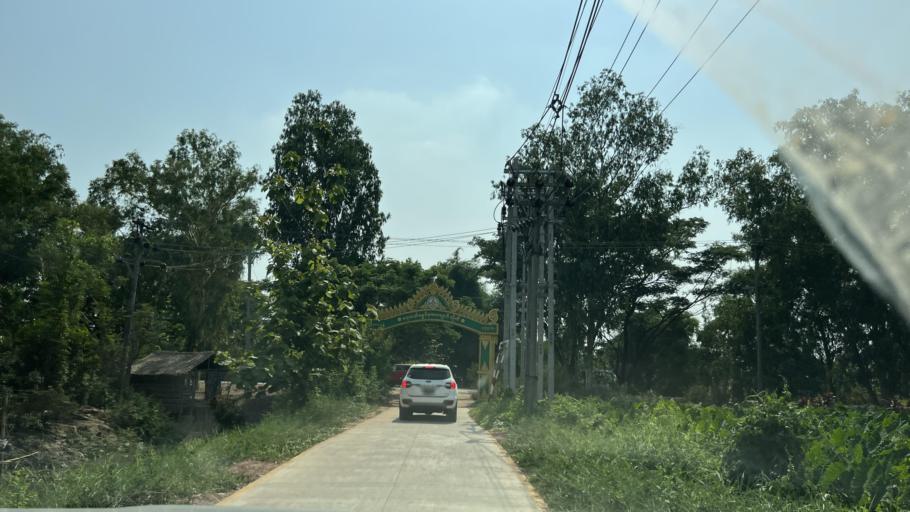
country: MM
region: Yangon
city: Twante
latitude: 16.9178
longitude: 95.9727
